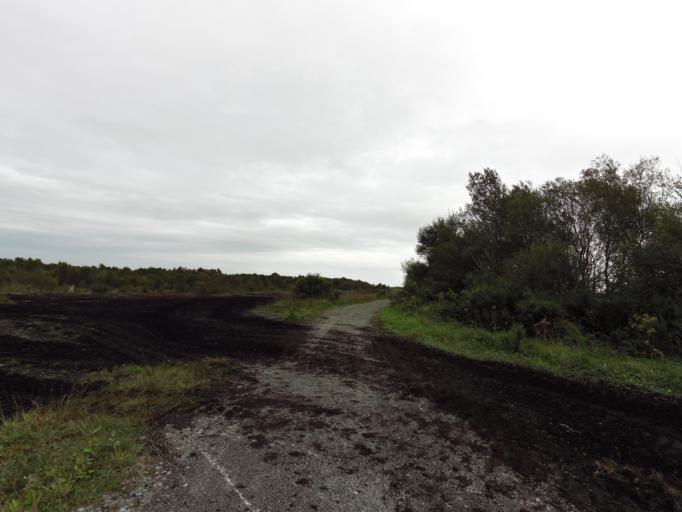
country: IE
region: Leinster
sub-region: Uibh Fhaili
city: Ferbane
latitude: 53.2351
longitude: -7.7682
